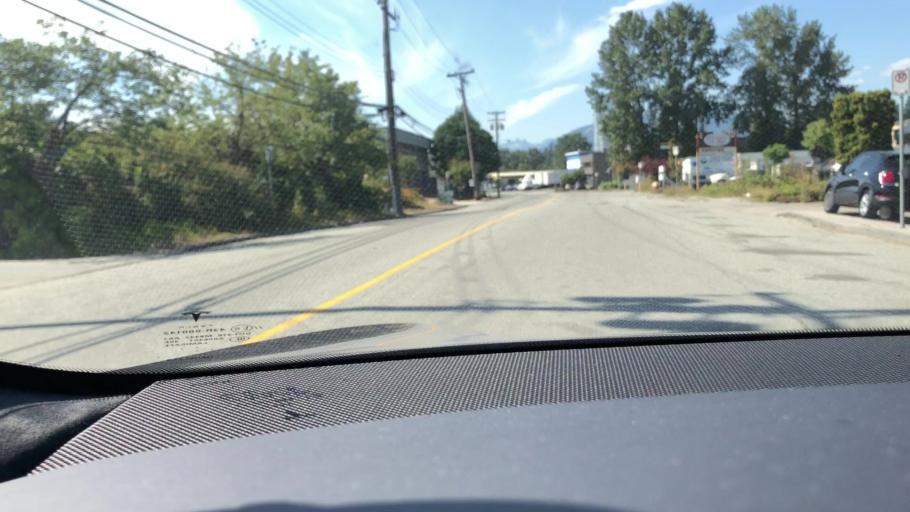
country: CA
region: British Columbia
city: Burnaby
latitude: 49.2568
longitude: -122.9770
